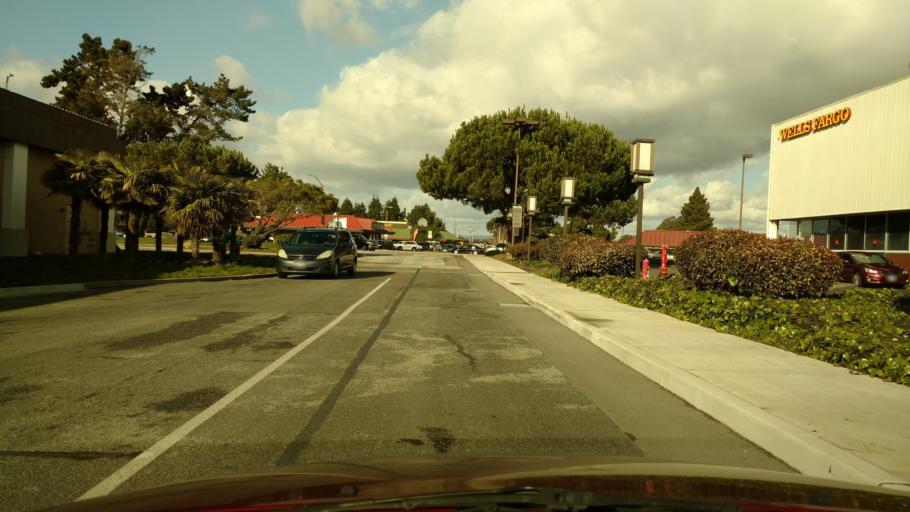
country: US
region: California
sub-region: Monterey County
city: Boronda
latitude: 36.7209
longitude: -121.6569
